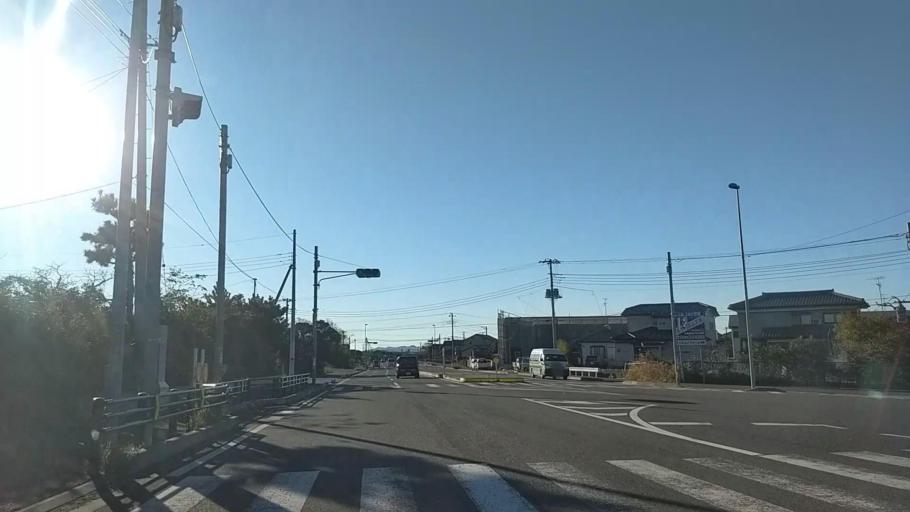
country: JP
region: Chiba
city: Kisarazu
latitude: 35.4033
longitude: 139.9195
